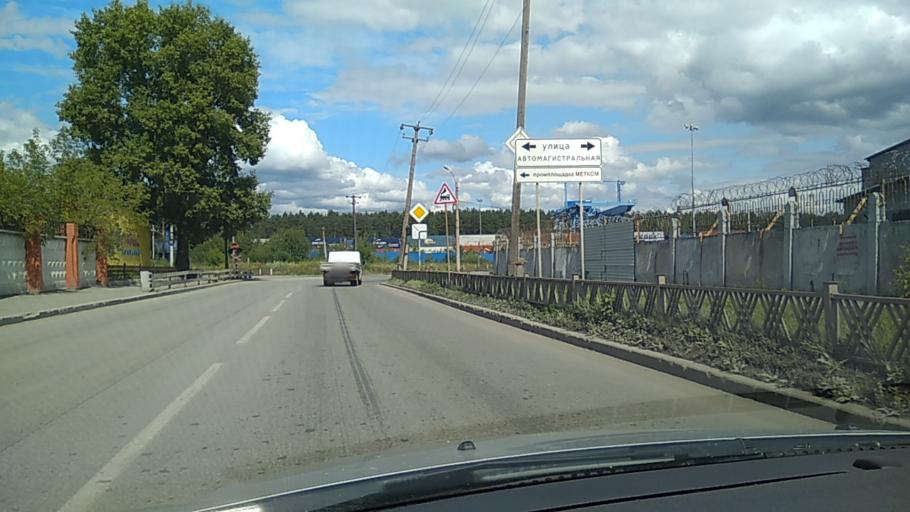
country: RU
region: Sverdlovsk
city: Shuvakish
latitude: 56.8871
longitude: 60.5366
